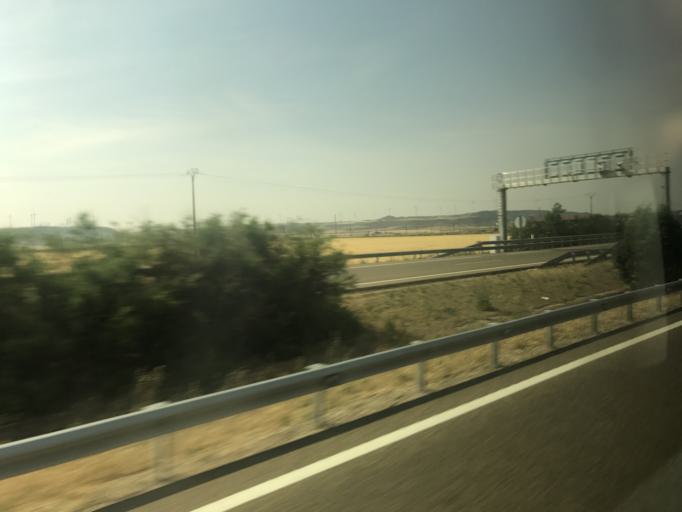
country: ES
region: Castille and Leon
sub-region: Provincia de Palencia
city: Quintana del Puente
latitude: 42.0719
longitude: -4.2169
